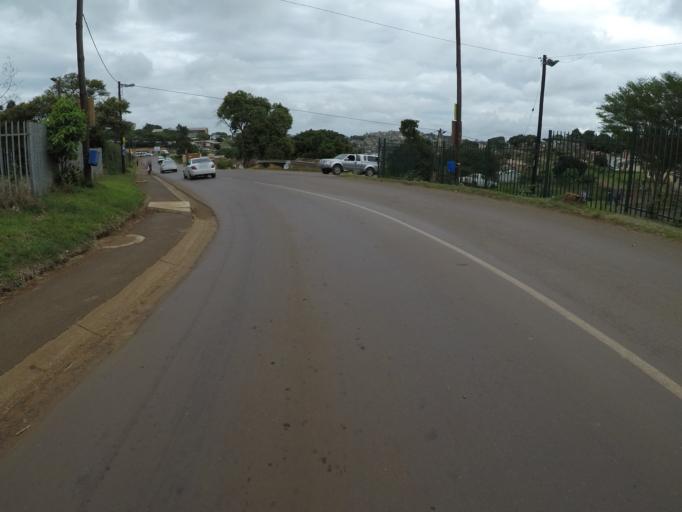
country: ZA
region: KwaZulu-Natal
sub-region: uThungulu District Municipality
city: Empangeni
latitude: -28.7752
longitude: 31.8650
